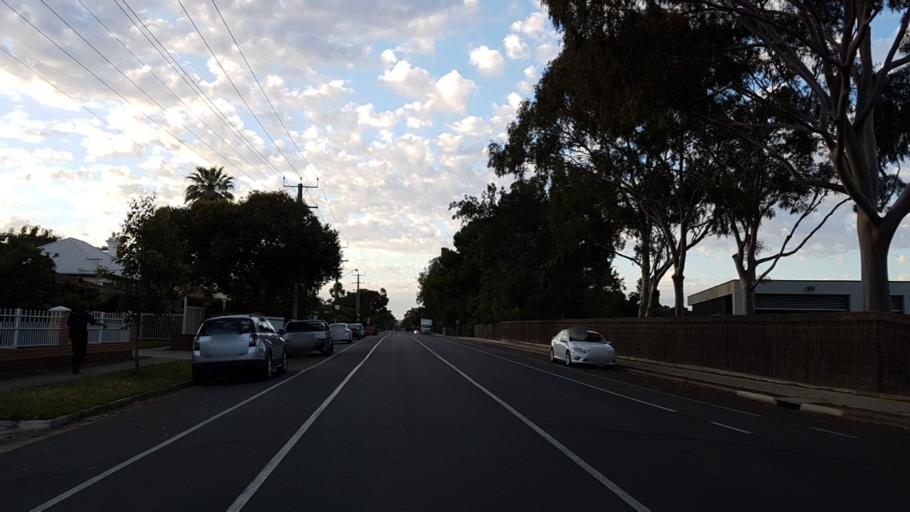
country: AU
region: South Australia
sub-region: City of West Torrens
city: Plympton
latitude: -34.9284
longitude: 138.5343
